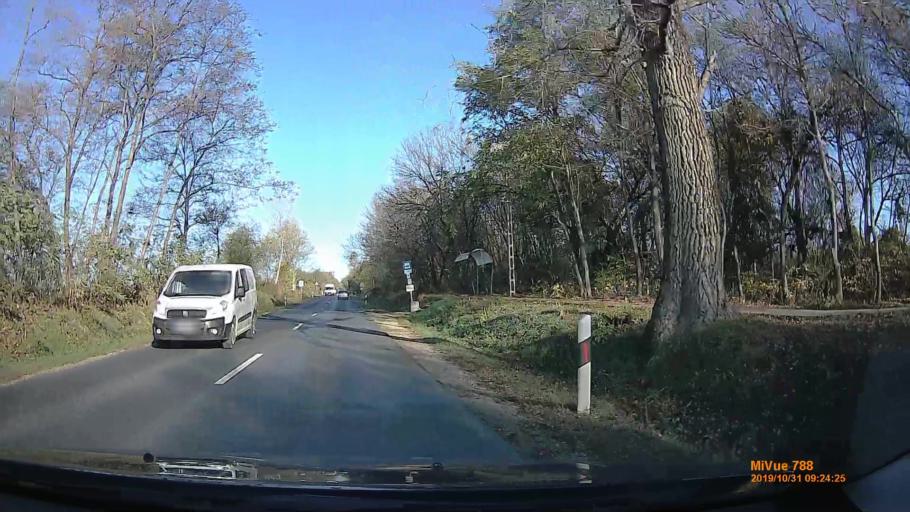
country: HU
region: Pest
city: Maglod
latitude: 47.4336
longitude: 19.3786
